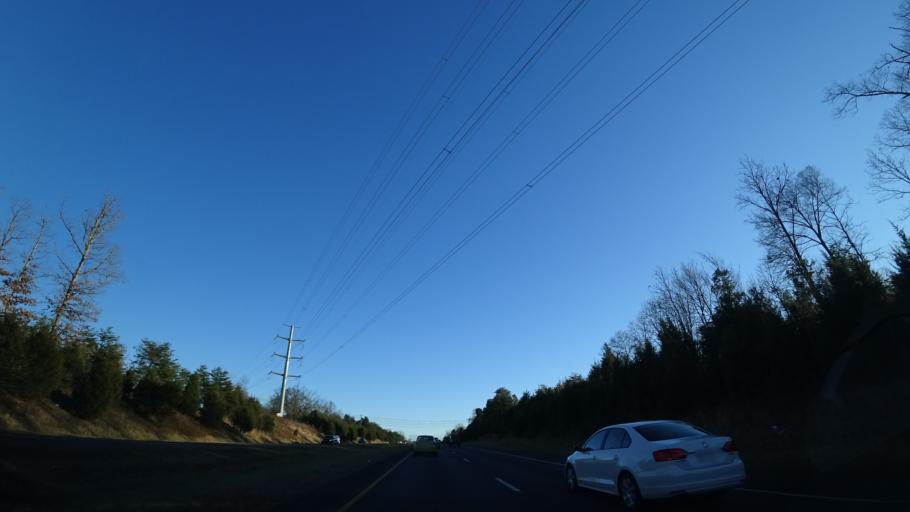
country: US
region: Virginia
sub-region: Prince William County
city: Bull Run
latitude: 38.7782
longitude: -77.5437
